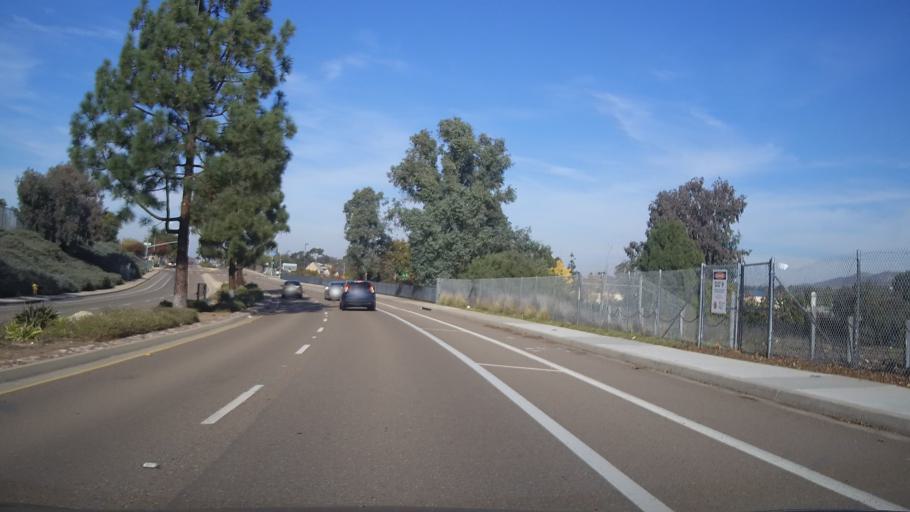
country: US
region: California
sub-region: San Diego County
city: La Mesa
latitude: 32.8180
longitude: -117.1041
